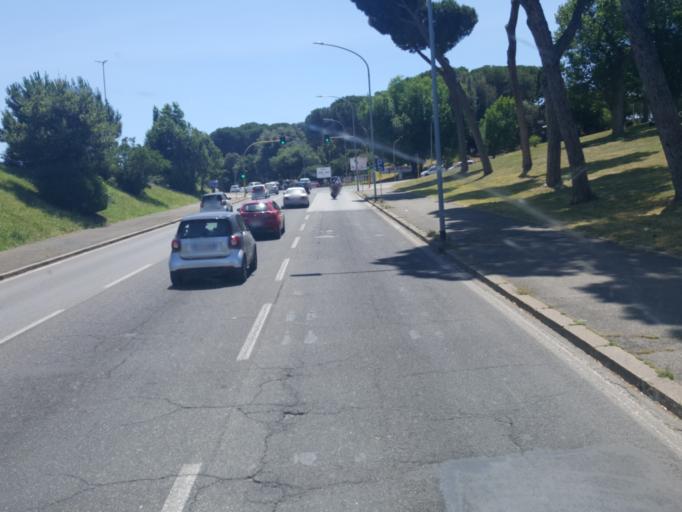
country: IT
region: Latium
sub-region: Citta metropolitana di Roma Capitale
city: Selcetta
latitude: 41.8256
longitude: 12.4648
